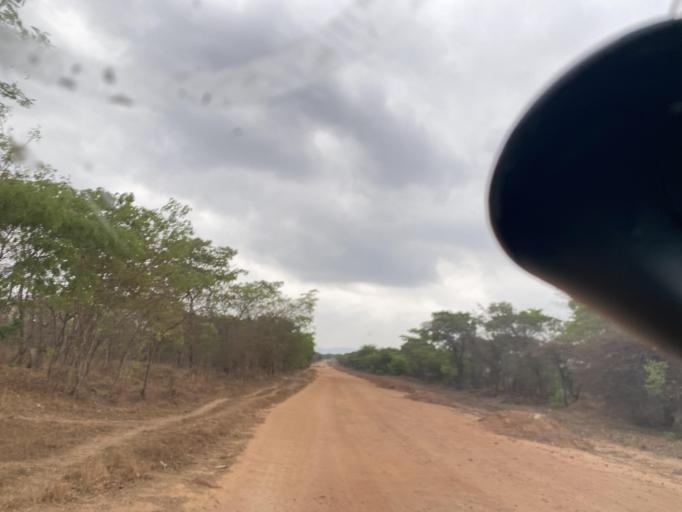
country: ZM
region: Lusaka
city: Chongwe
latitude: -15.2687
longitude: 28.7318
